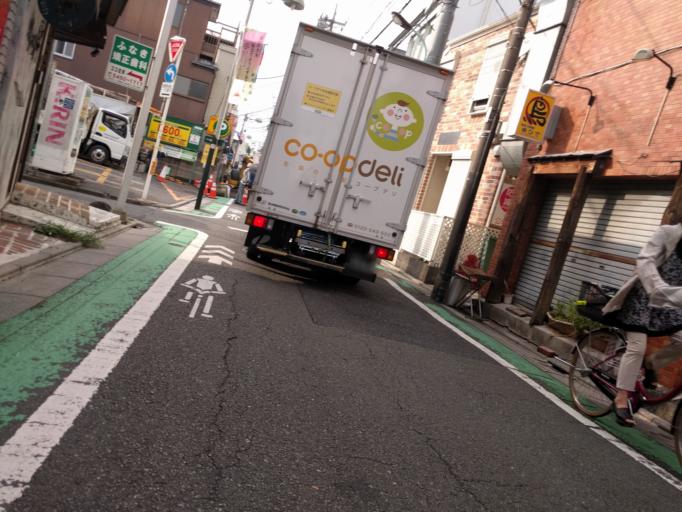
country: JP
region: Tokyo
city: Tokyo
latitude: 35.6549
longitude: 139.6322
